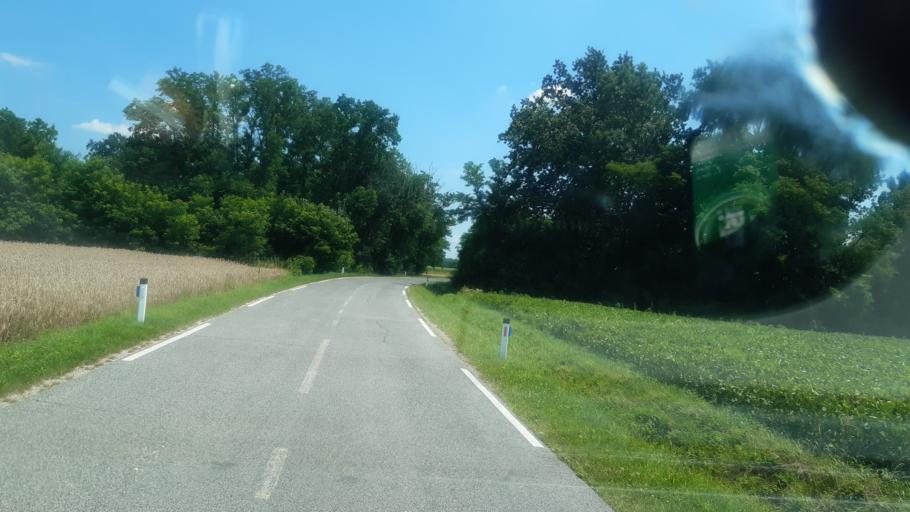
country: SI
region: Beltinci
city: Gancani
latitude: 46.6613
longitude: 16.2428
